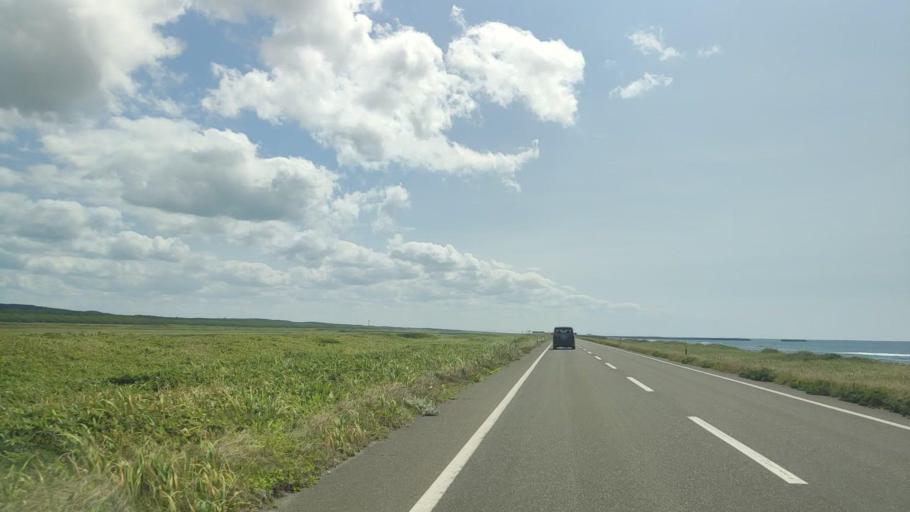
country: JP
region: Hokkaido
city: Wakkanai
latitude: 45.1008
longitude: 141.6214
